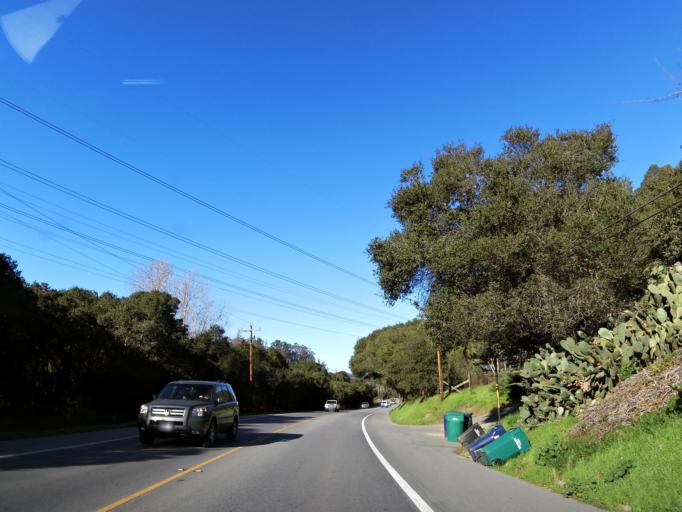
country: US
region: California
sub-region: Monterey County
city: Las Lomas
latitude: 36.8463
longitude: -121.6900
